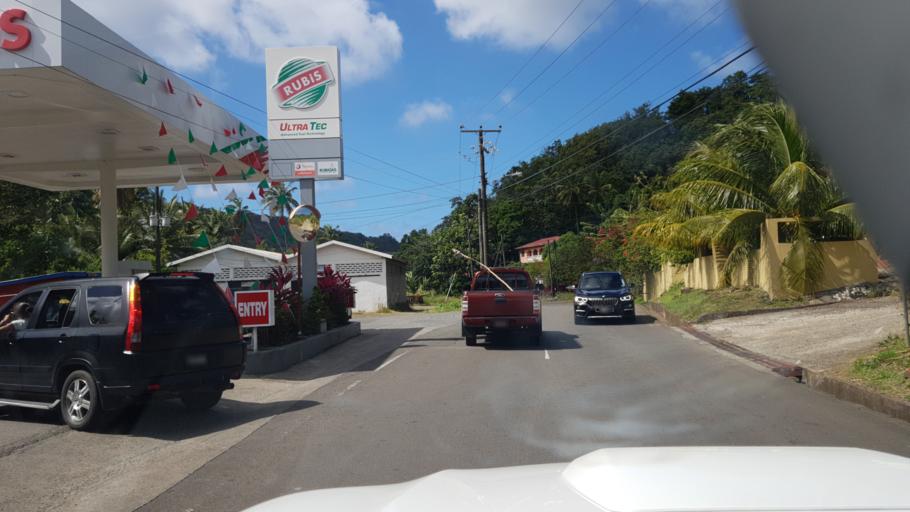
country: LC
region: Castries Quarter
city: Bisee
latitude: 14.0172
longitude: -60.9584
